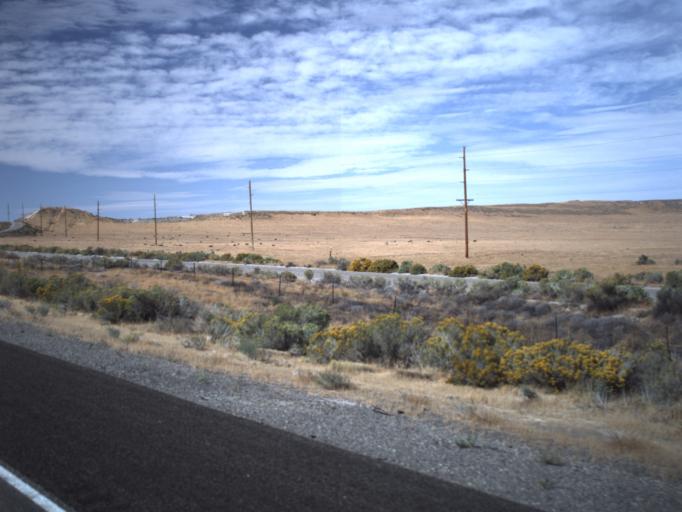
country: US
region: Utah
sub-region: Tooele County
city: Grantsville
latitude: 40.7739
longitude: -112.9768
